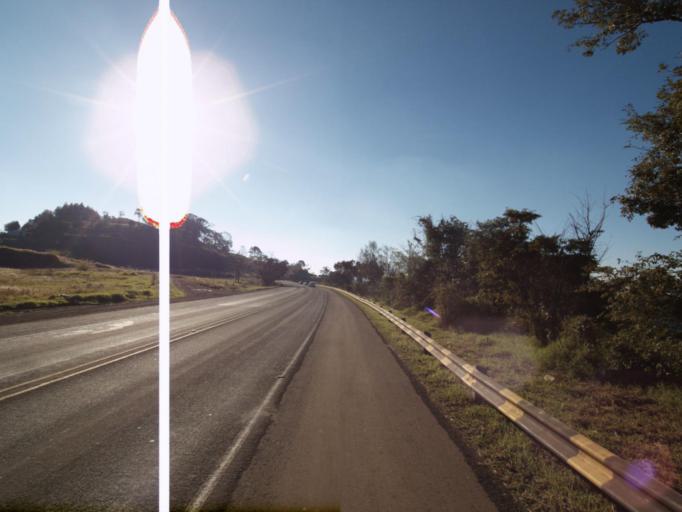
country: BR
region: Santa Catarina
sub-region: Chapeco
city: Chapeco
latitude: -26.9808
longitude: -52.7352
